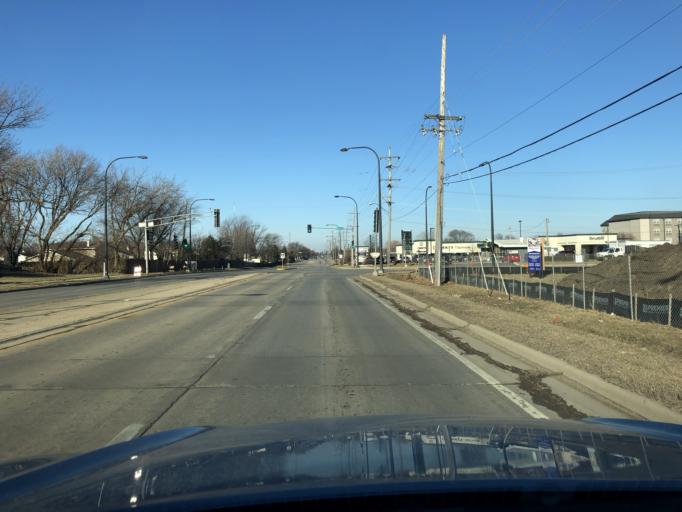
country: US
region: Illinois
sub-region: DuPage County
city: Itasca
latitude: 41.9920
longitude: -88.0313
